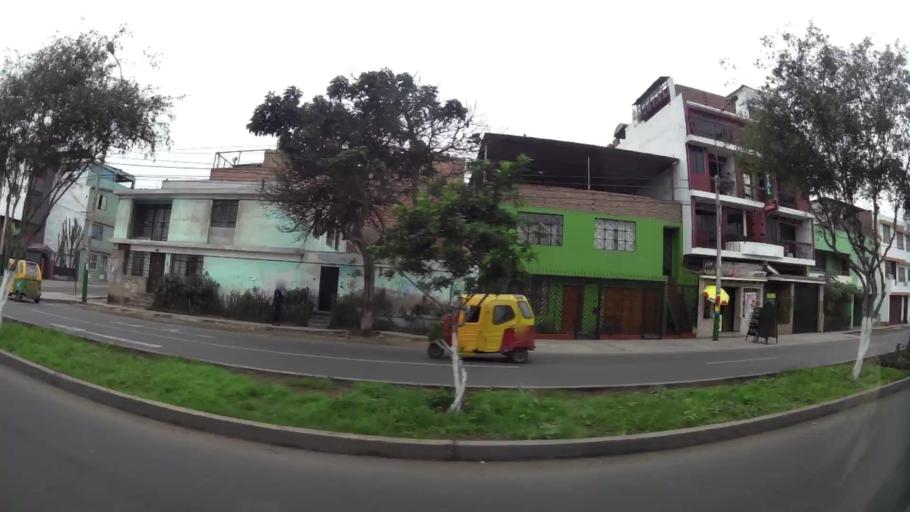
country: PE
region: Lima
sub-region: Lima
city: Surco
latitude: -12.1599
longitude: -76.9694
